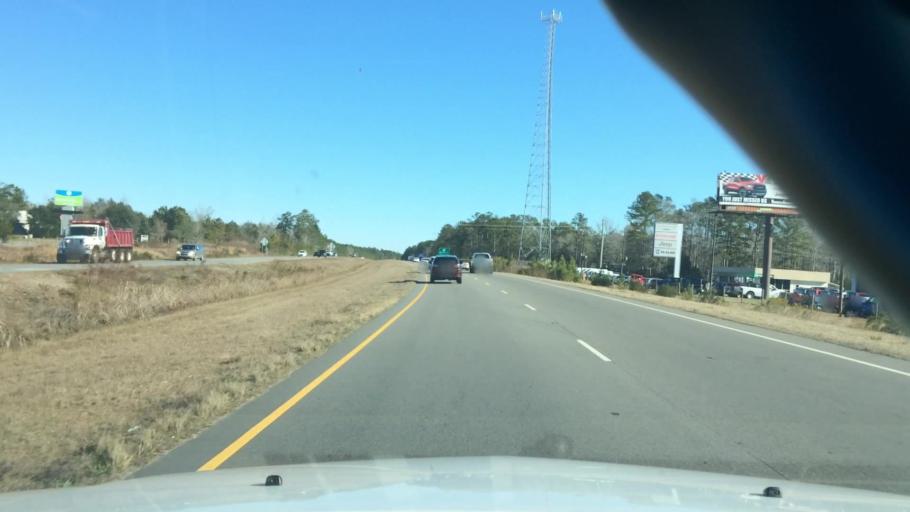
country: US
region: North Carolina
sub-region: Brunswick County
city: Shallotte
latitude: 33.9620
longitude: -78.4168
